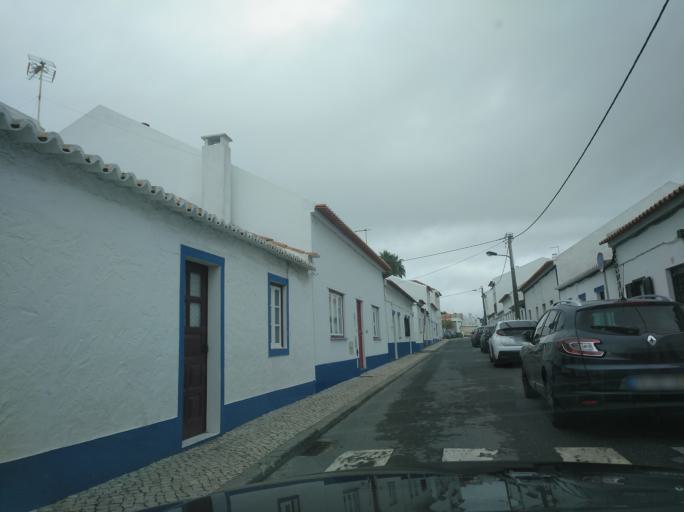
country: PT
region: Setubal
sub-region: Sines
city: Porto Covo
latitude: 37.8510
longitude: -8.7916
